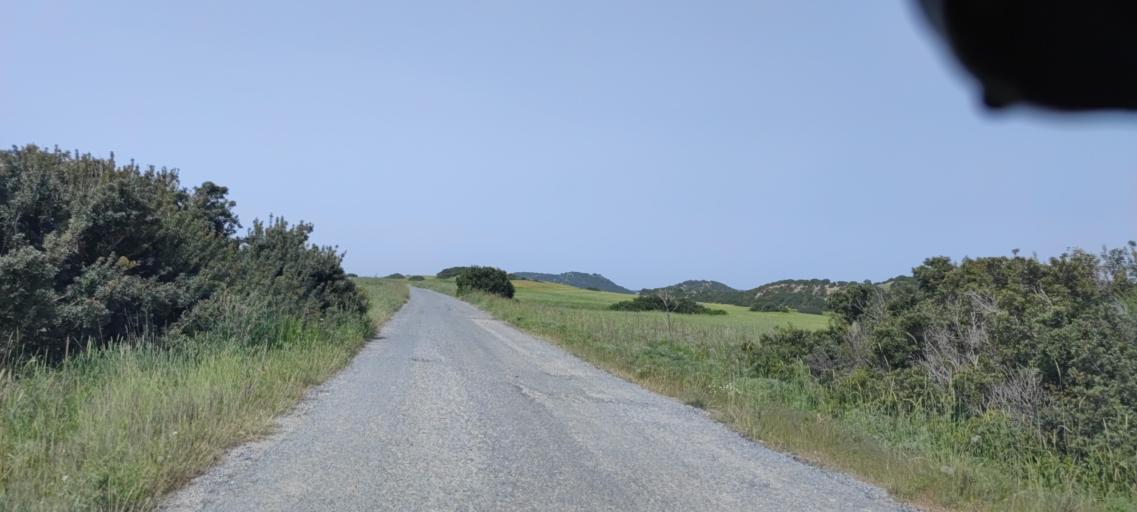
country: CY
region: Ammochostos
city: Rizokarpaso
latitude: 35.6448
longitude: 34.5319
